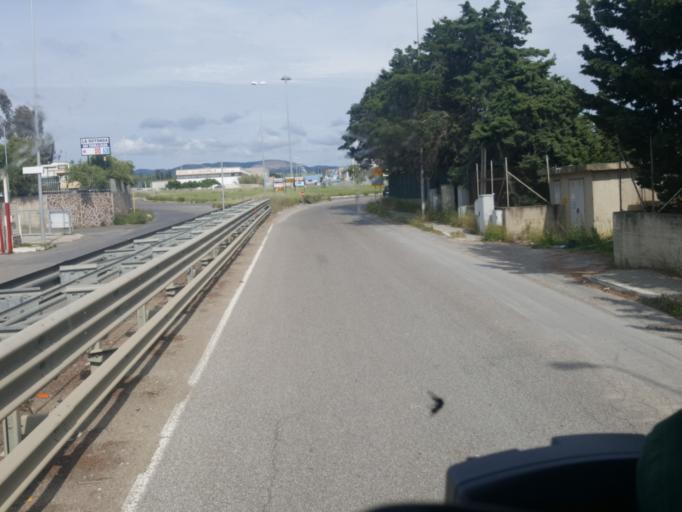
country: IT
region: Latium
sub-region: Citta metropolitana di Roma Capitale
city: Aurelia
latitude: 42.1200
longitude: 11.7768
